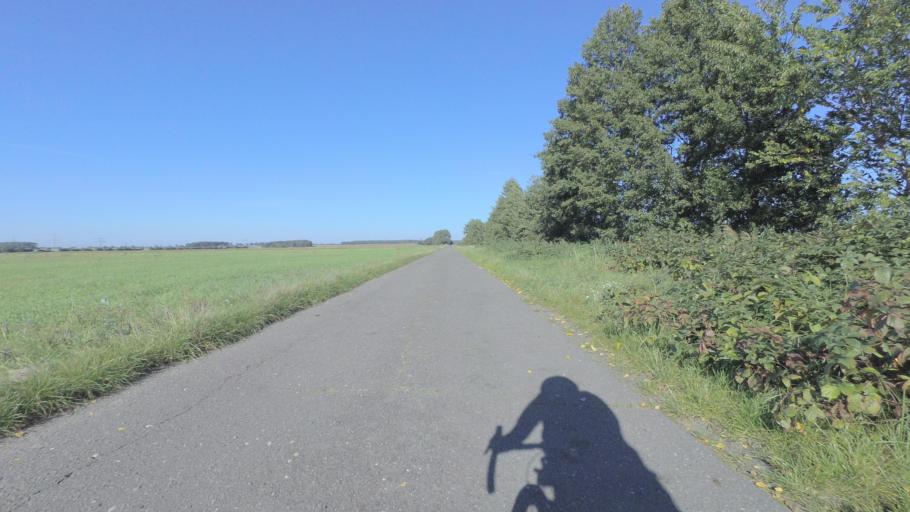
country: DE
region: Brandenburg
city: Am Mellensee
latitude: 52.2102
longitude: 13.3397
